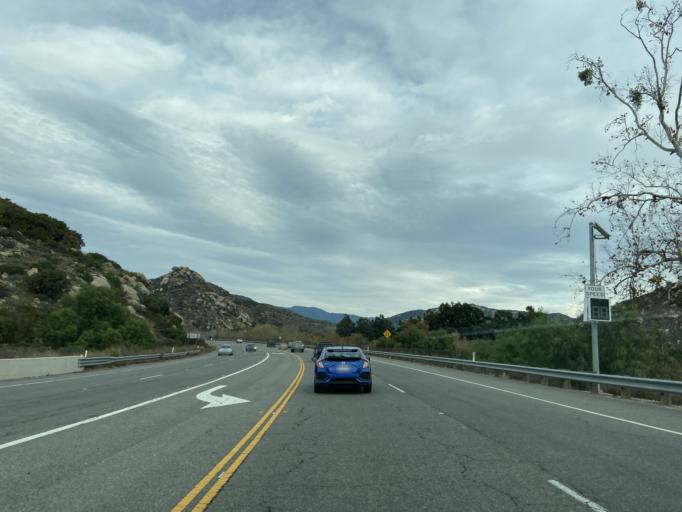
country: US
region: California
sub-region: San Diego County
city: Rainbow
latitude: 33.3367
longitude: -117.1463
